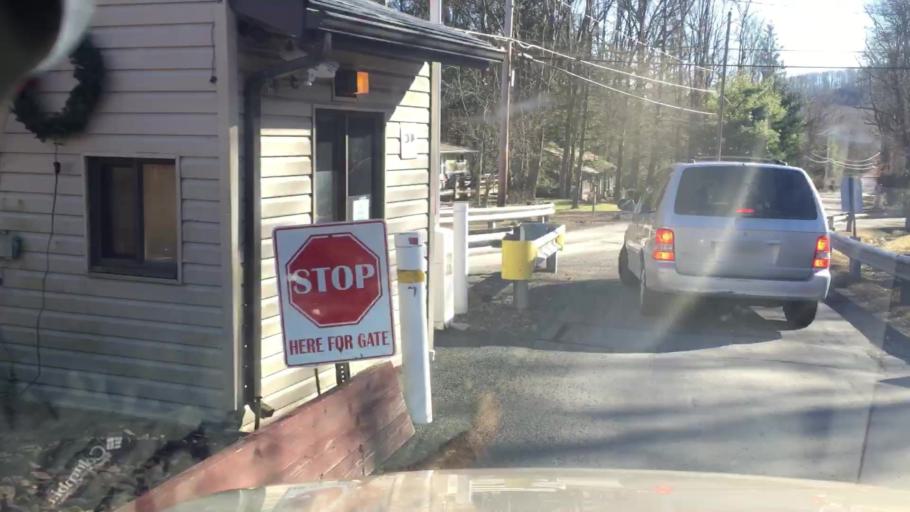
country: US
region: Pennsylvania
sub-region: Luzerne County
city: White Haven
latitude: 41.0410
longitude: -75.8145
